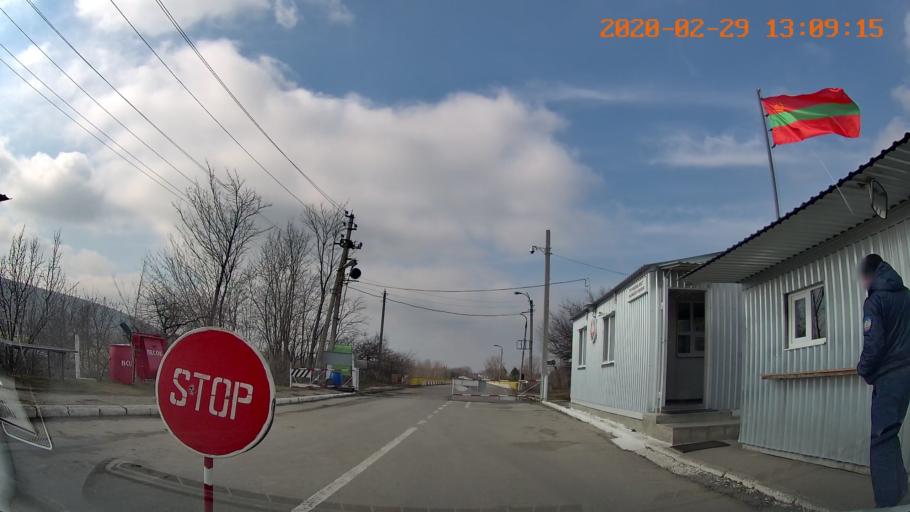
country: MD
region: Telenesti
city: Camenca
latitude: 48.0110
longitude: 28.7045
